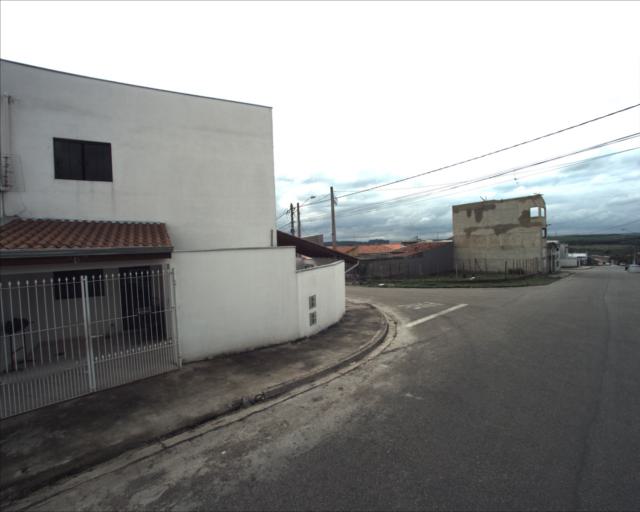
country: BR
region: Sao Paulo
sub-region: Sorocaba
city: Sorocaba
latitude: -23.4250
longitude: -47.4665
